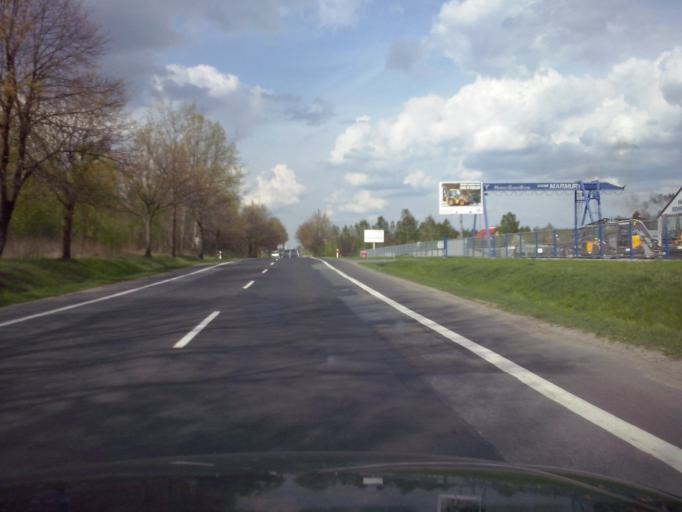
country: PL
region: Subcarpathian Voivodeship
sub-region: Powiat rzeszowski
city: Sokolow Malopolski
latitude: 50.2384
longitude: 22.1251
